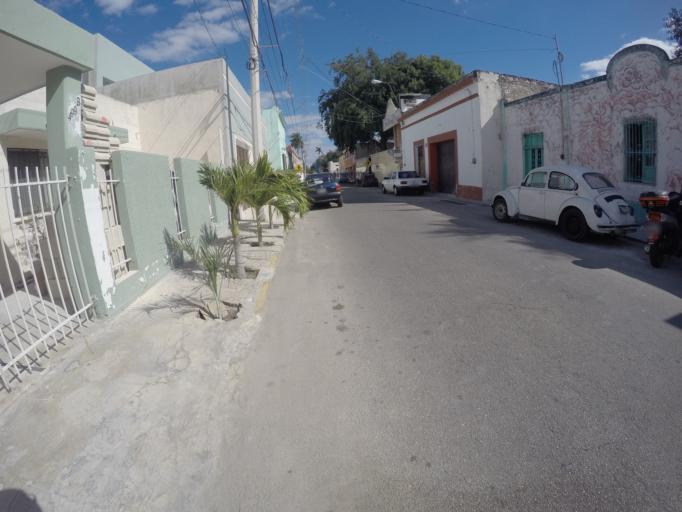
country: MX
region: Yucatan
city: Merida
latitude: 20.9805
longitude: -89.6201
